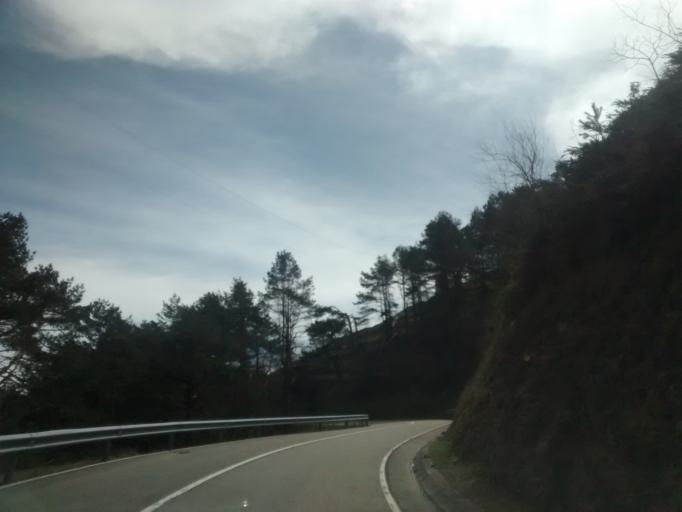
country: ES
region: Cantabria
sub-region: Provincia de Cantabria
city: Vega de Pas
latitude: 43.1808
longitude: -3.8015
